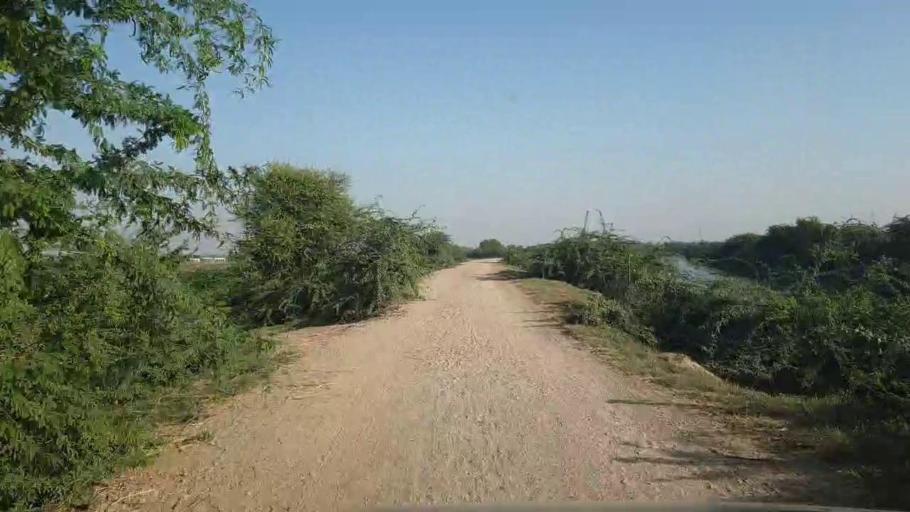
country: PK
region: Sindh
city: Badin
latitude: 24.6952
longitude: 68.8161
